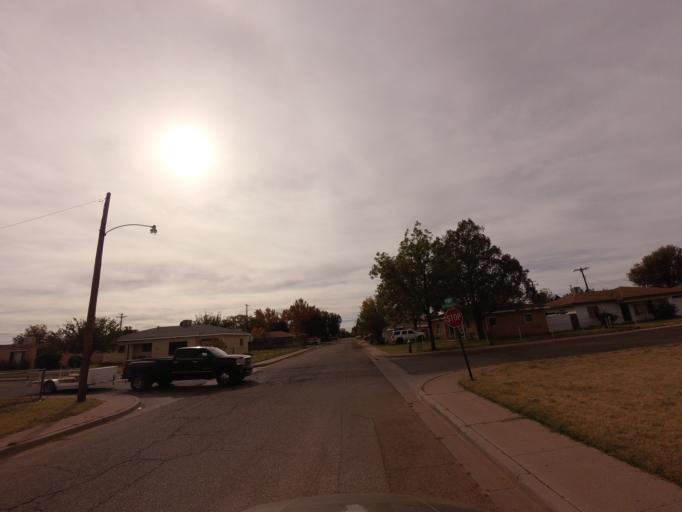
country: US
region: New Mexico
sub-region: Curry County
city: Clovis
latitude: 34.4271
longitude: -103.2095
